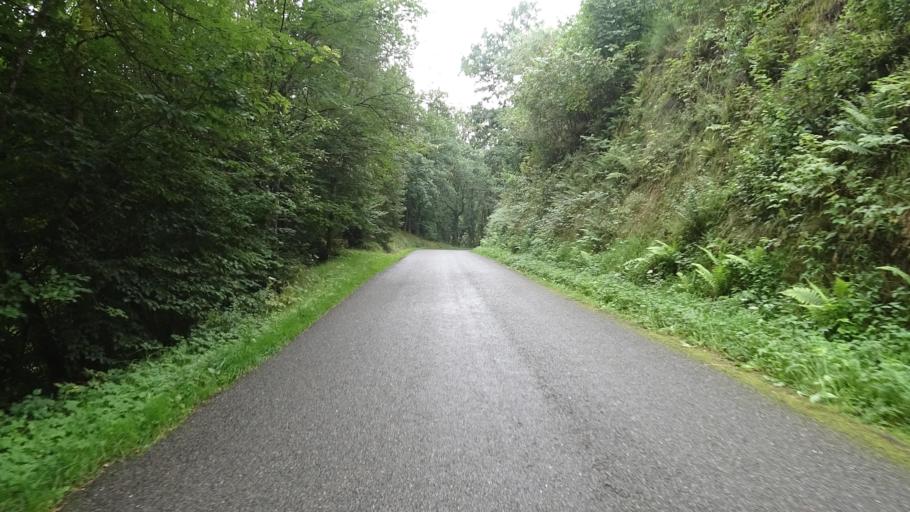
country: BE
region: Wallonia
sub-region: Province du Luxembourg
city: Chiny
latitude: 49.7896
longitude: 5.3750
